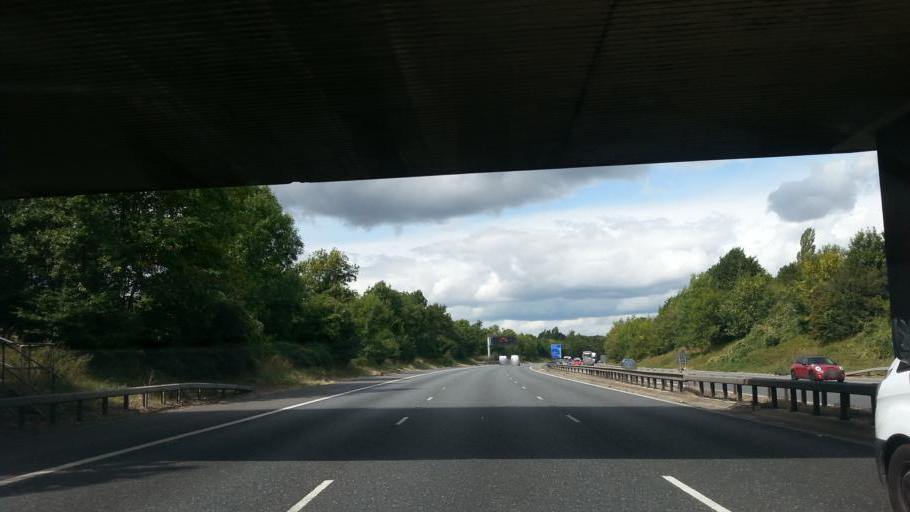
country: GB
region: England
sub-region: Essex
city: Little Hallingbury
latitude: 51.8438
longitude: 0.1888
